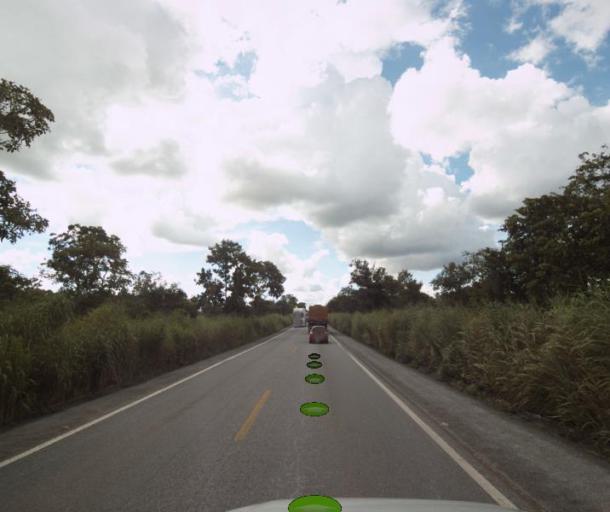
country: BR
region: Goias
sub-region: Porangatu
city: Porangatu
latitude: -13.1876
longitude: -49.1643
